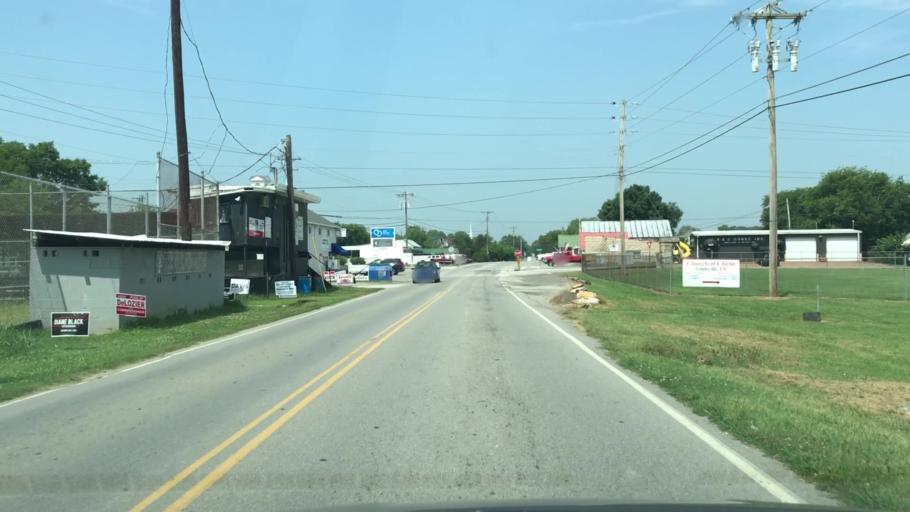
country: US
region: Tennessee
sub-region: Wilson County
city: Rural Hill
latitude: 36.1127
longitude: -86.4145
